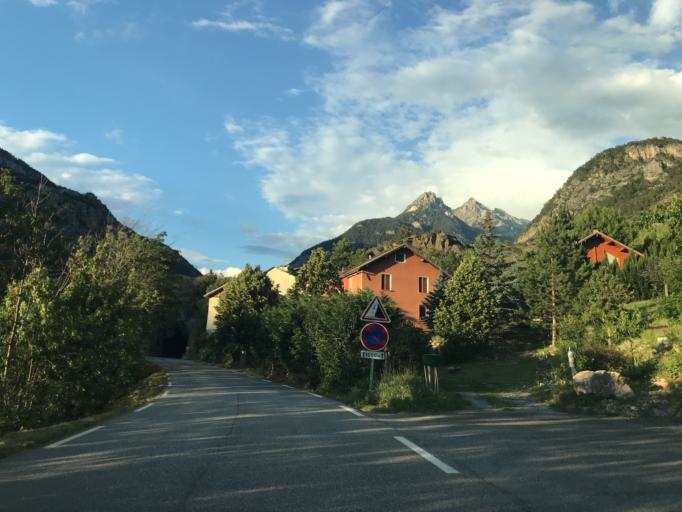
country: FR
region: Provence-Alpes-Cote d'Azur
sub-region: Departement des Hautes-Alpes
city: Guillestre
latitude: 44.6676
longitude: 6.6737
